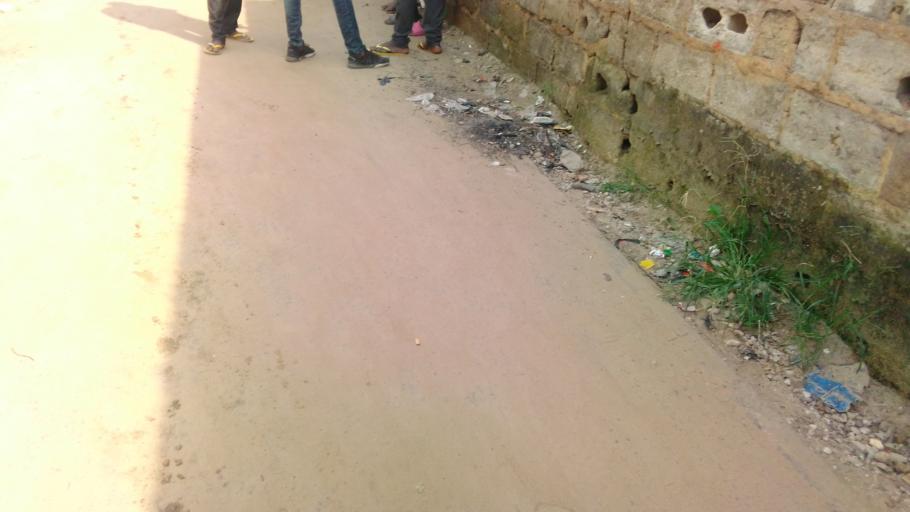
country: CD
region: Kinshasa
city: Masina
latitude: -4.3970
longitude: 15.3445
